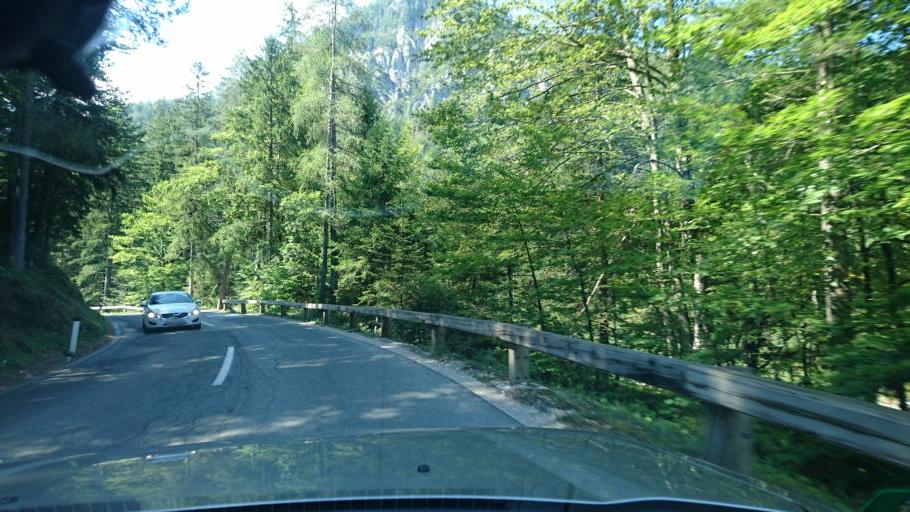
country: SI
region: Kranjska Gora
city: Kranjska Gora
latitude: 46.4688
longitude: 13.7831
